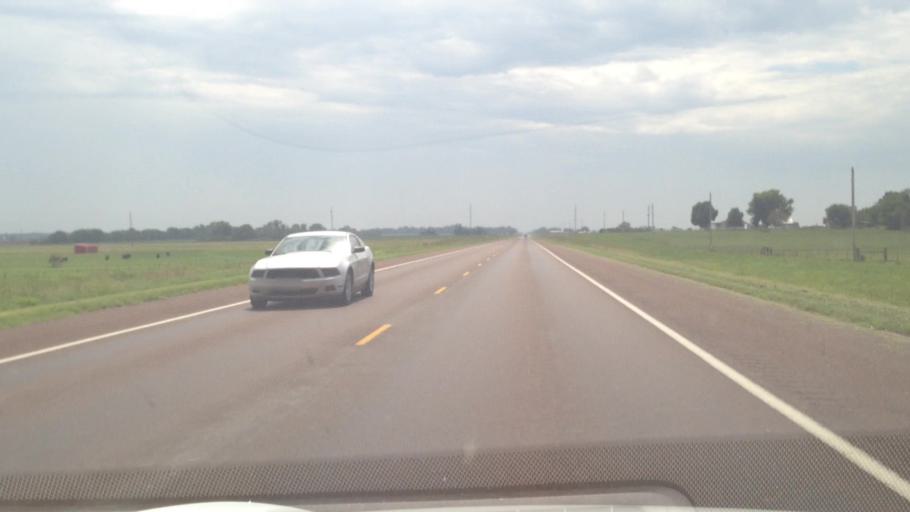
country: US
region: Kansas
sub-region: Crawford County
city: Girard
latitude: 37.4615
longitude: -94.8330
